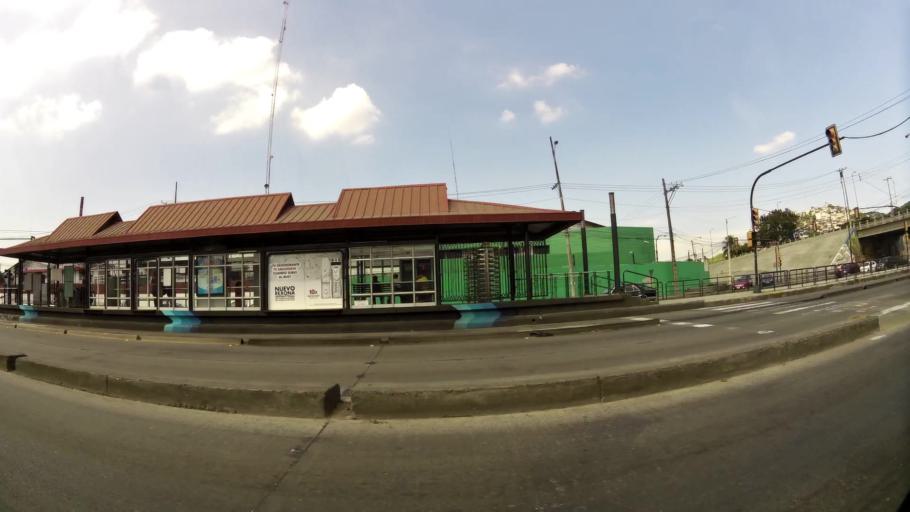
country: EC
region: Guayas
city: Guayaquil
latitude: -2.1394
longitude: -79.9343
